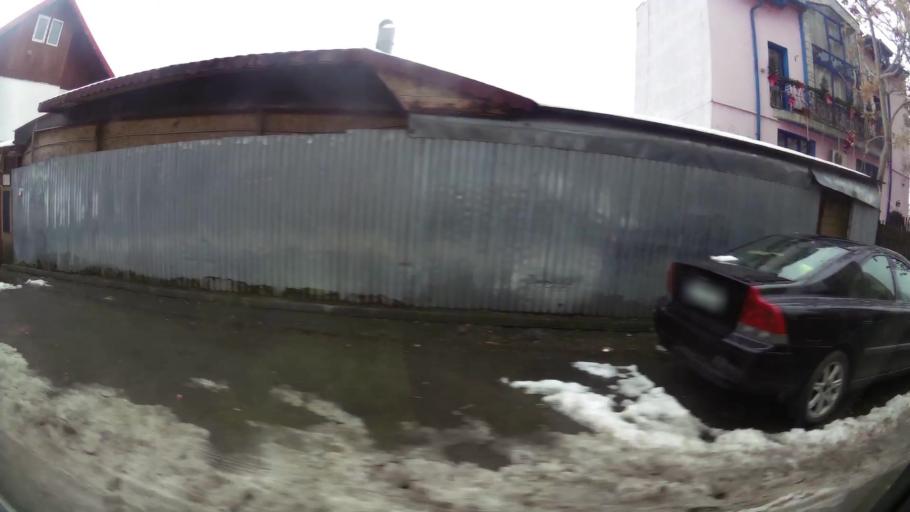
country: RO
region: Ilfov
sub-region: Comuna Popesti-Leordeni
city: Popesti-Leordeni
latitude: 44.4088
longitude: 26.1678
